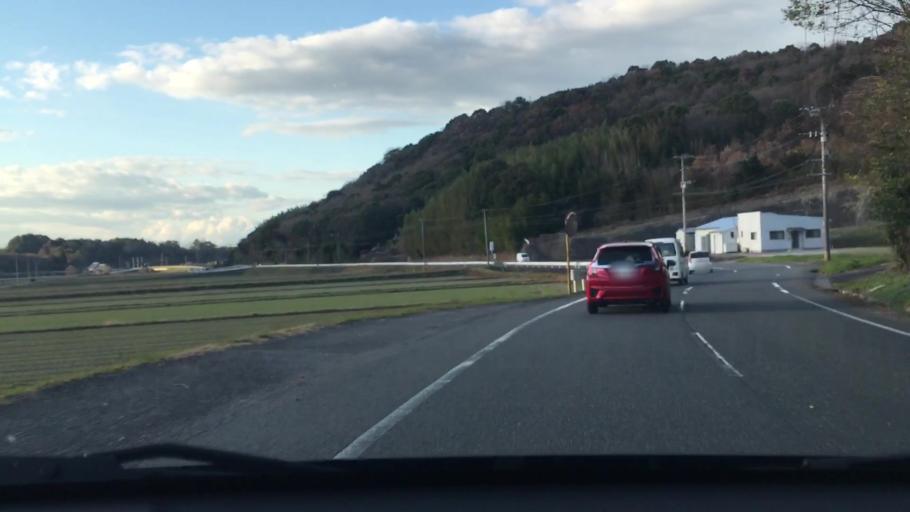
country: JP
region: Oita
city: Bungo-Takada-shi
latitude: 33.5089
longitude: 131.3590
